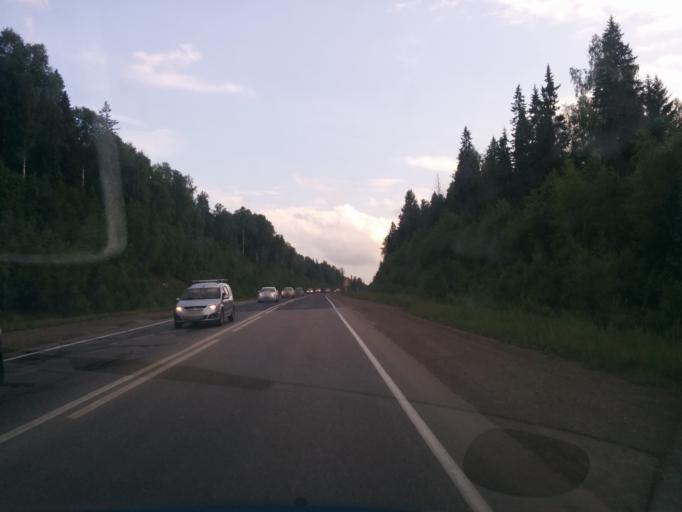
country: RU
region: Perm
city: Novyye Lyady
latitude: 58.0838
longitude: 56.4299
